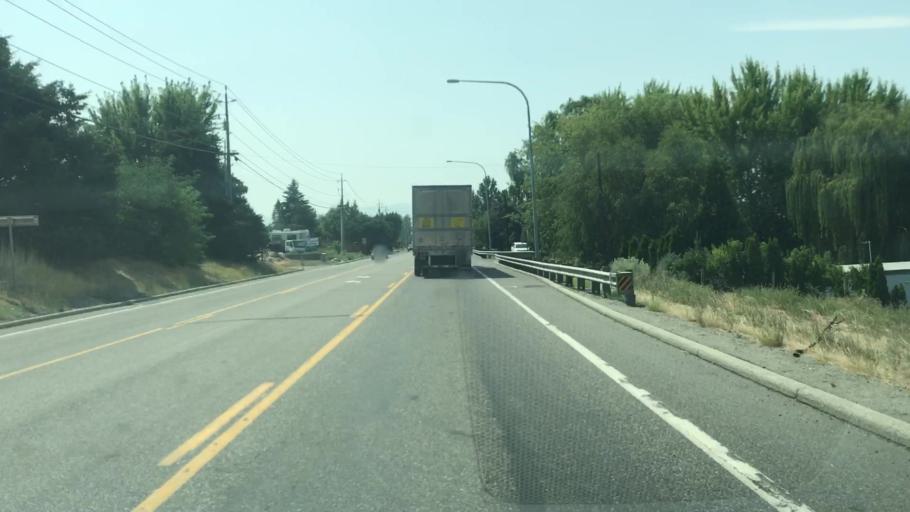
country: US
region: Washington
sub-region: Douglas County
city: East Wenatchee Bench
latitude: 47.4491
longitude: -120.2974
